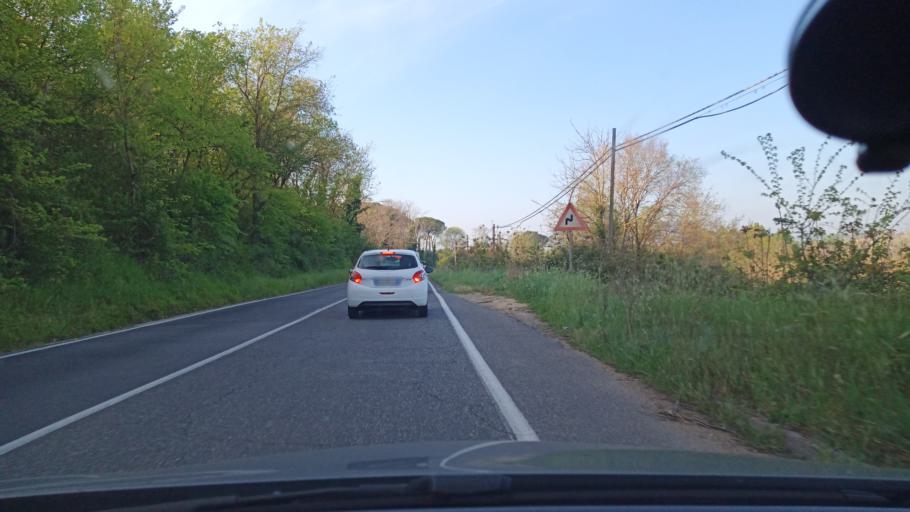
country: IT
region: Latium
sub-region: Citta metropolitana di Roma Capitale
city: Fiano Romano
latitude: 42.1740
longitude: 12.6360
